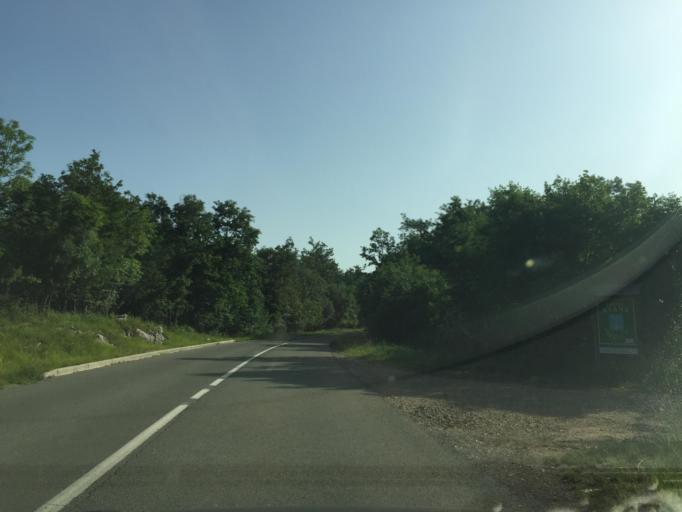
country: HR
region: Primorsko-Goranska
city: Kastav
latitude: 45.4191
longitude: 14.3164
